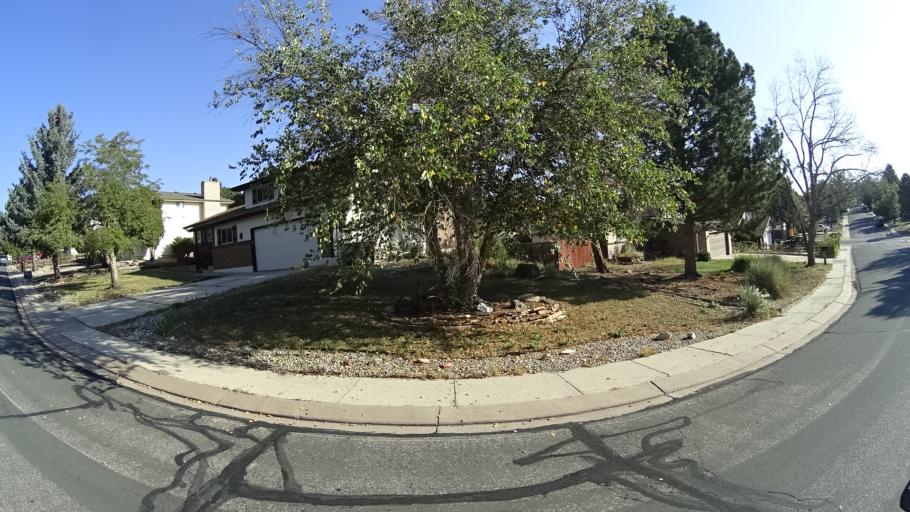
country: US
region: Colorado
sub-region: El Paso County
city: Cimarron Hills
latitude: 38.8854
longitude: -104.7308
